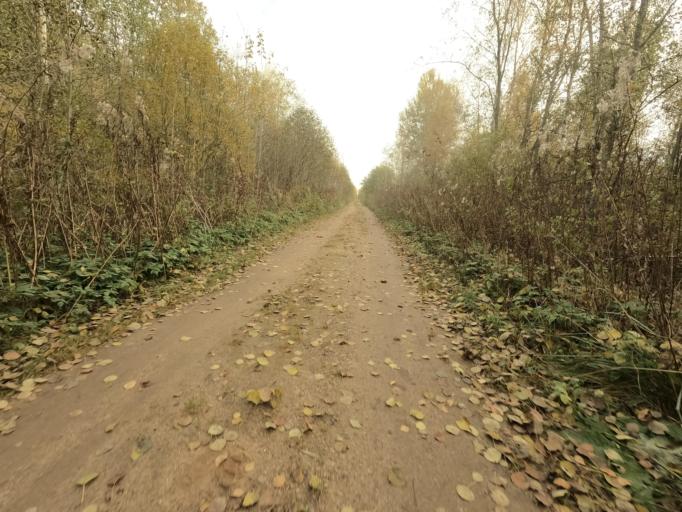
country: RU
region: Novgorod
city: Batetskiy
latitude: 58.8796
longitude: 30.7912
